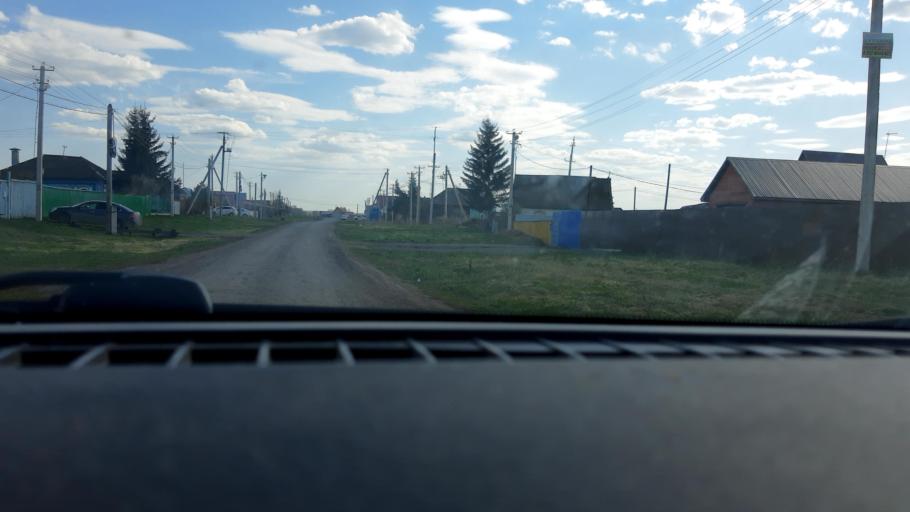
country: RU
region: Bashkortostan
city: Ufa
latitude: 54.5519
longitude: 55.9516
